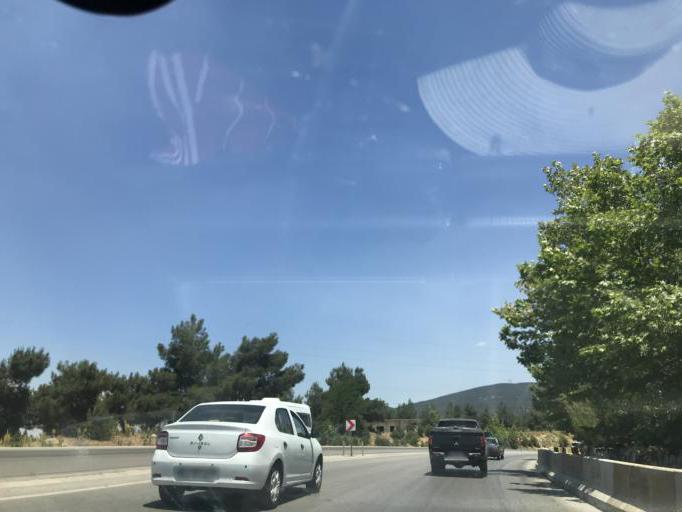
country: TR
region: Denizli
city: Honaz
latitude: 37.7325
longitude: 29.1788
